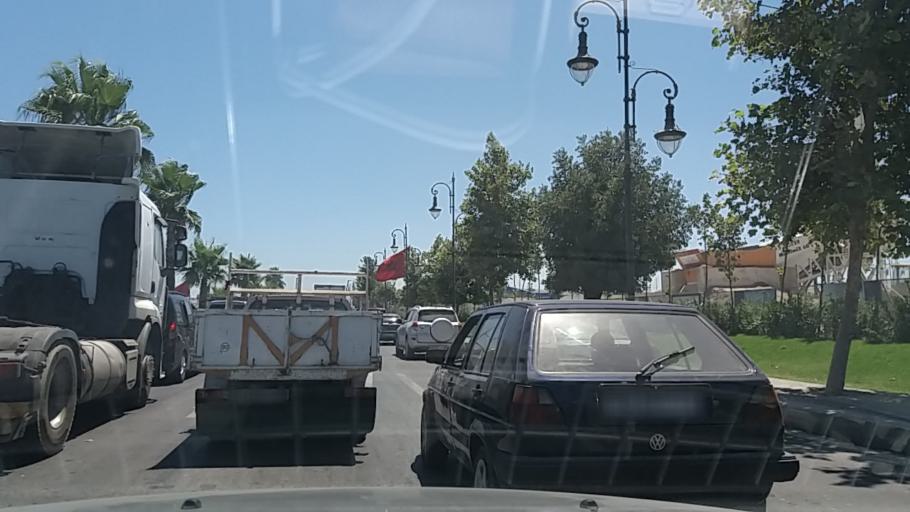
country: MA
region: Tanger-Tetouan
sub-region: Tanger-Assilah
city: Tangier
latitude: 35.7547
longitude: -5.7908
